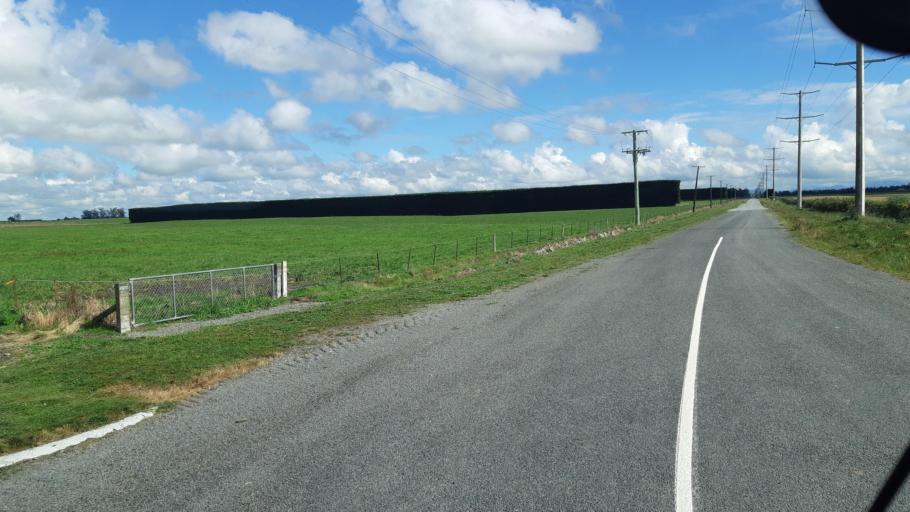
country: NZ
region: Canterbury
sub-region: Selwyn District
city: Darfield
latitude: -43.4728
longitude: 172.2585
